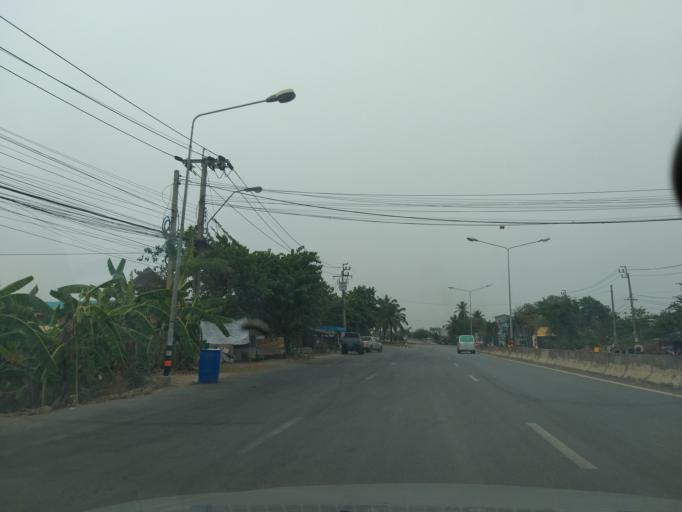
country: TH
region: Bangkok
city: Nong Chok
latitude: 13.8148
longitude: 100.9328
